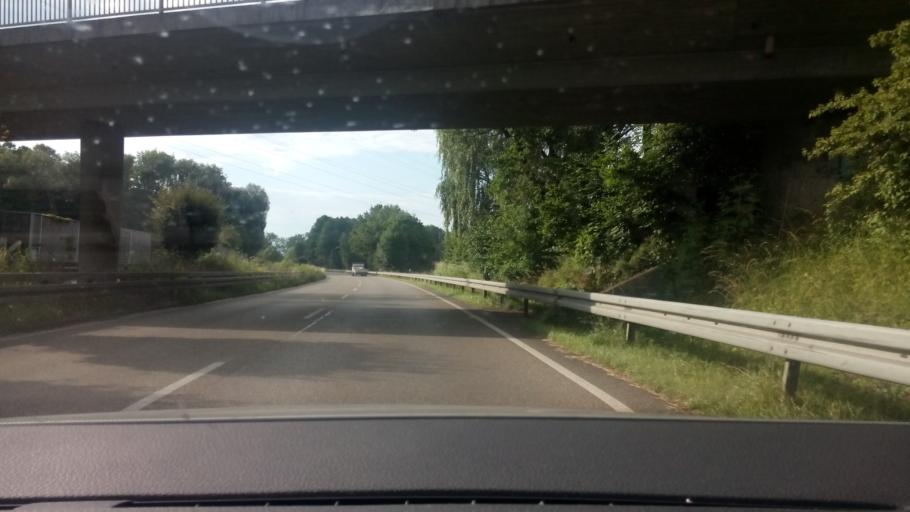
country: DE
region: Bavaria
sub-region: Upper Bavaria
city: Karlsfeld
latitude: 48.2320
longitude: 11.4537
